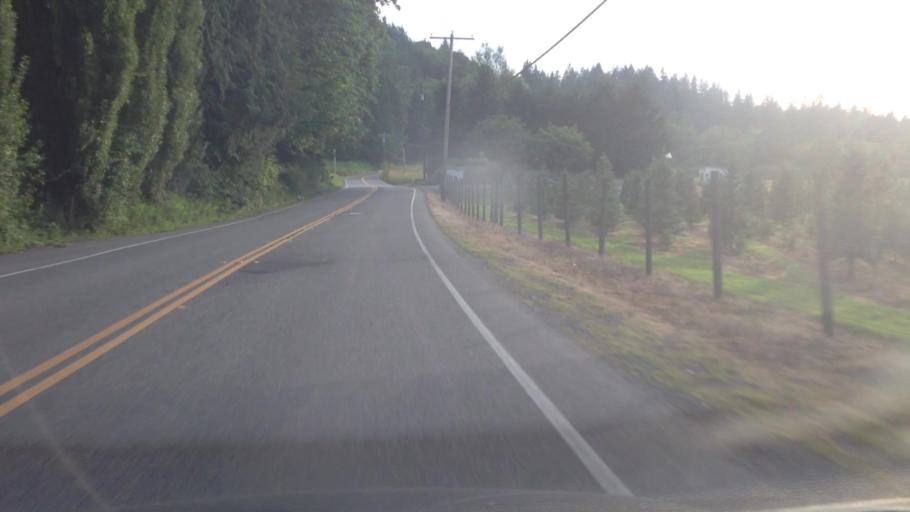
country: US
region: Washington
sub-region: King County
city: Duvall
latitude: 47.7432
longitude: -121.9425
